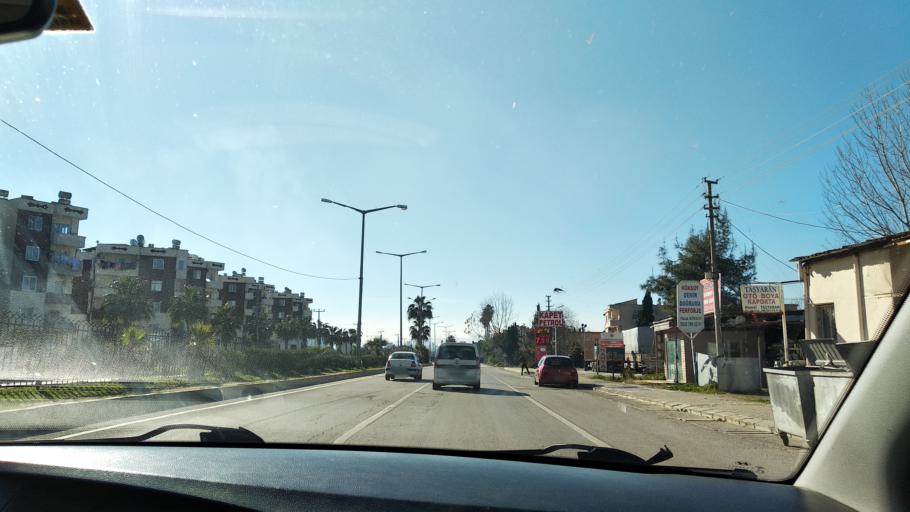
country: TR
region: Mersin
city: Tomuk
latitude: 36.6525
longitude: 34.3814
